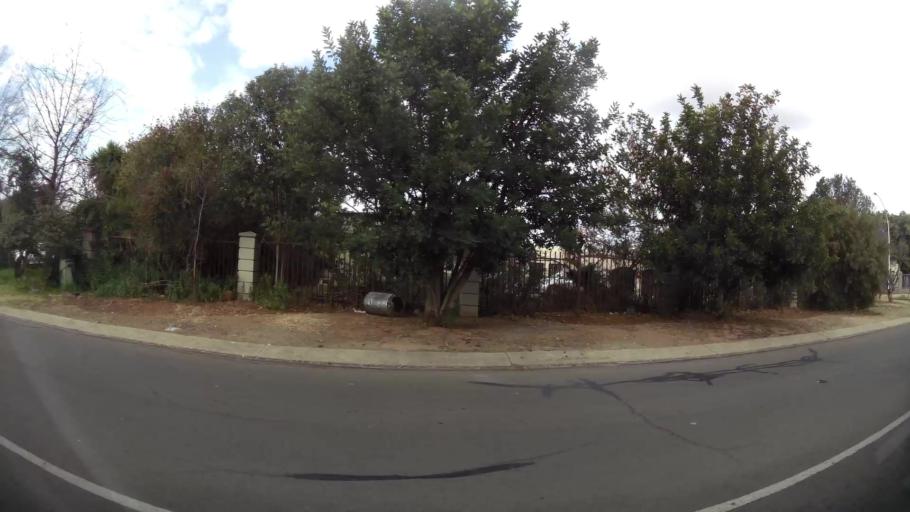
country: ZA
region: Orange Free State
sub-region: Mangaung Metropolitan Municipality
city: Bloemfontein
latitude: -29.0768
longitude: 26.2113
